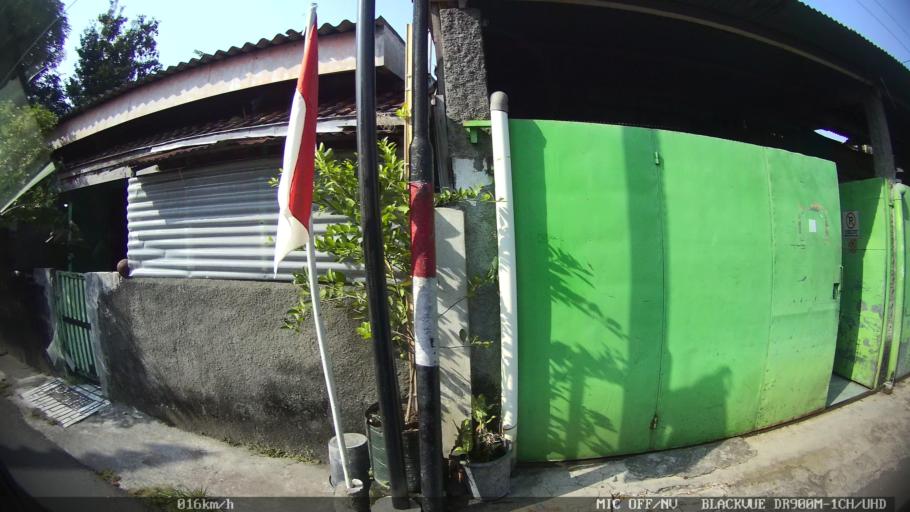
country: ID
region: Daerah Istimewa Yogyakarta
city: Yogyakarta
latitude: -7.8049
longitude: 110.3595
